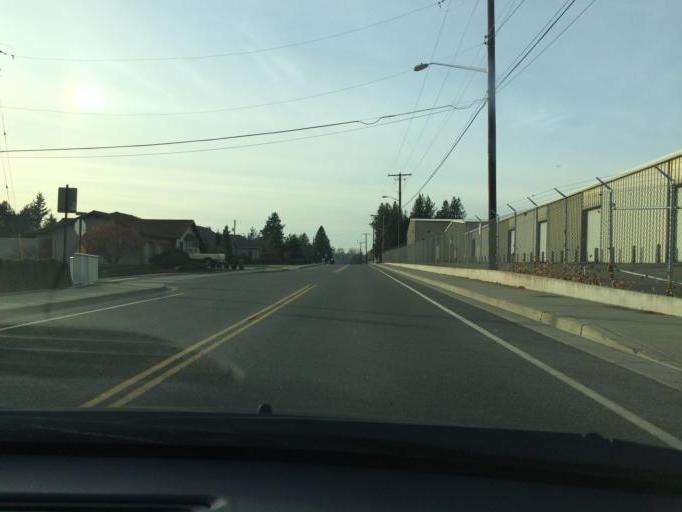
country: US
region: Washington
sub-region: Whatcom County
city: Lynden
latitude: 48.9357
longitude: -122.4744
